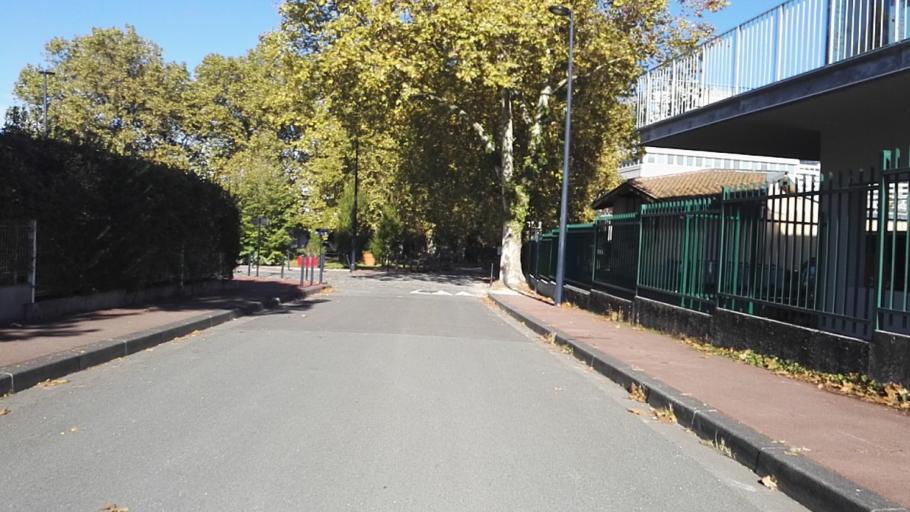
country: FR
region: Aquitaine
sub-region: Departement de la Gironde
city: Talence
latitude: 44.8233
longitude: -0.6079
